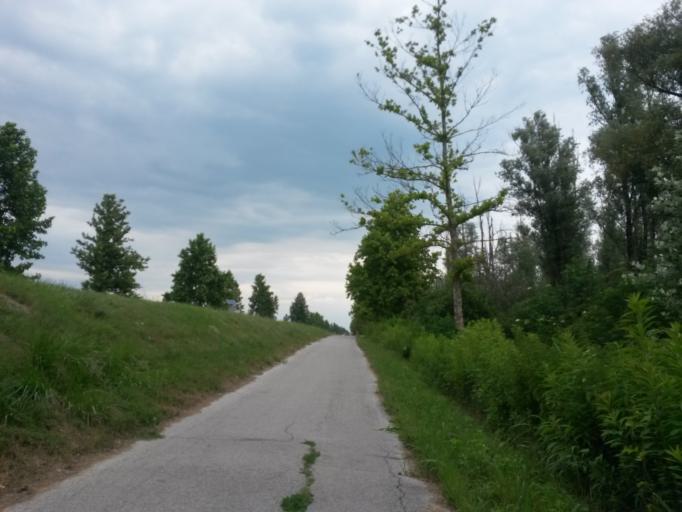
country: HR
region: Osjecko-Baranjska
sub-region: Grad Osijek
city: Bilje
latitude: 45.5794
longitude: 18.7218
